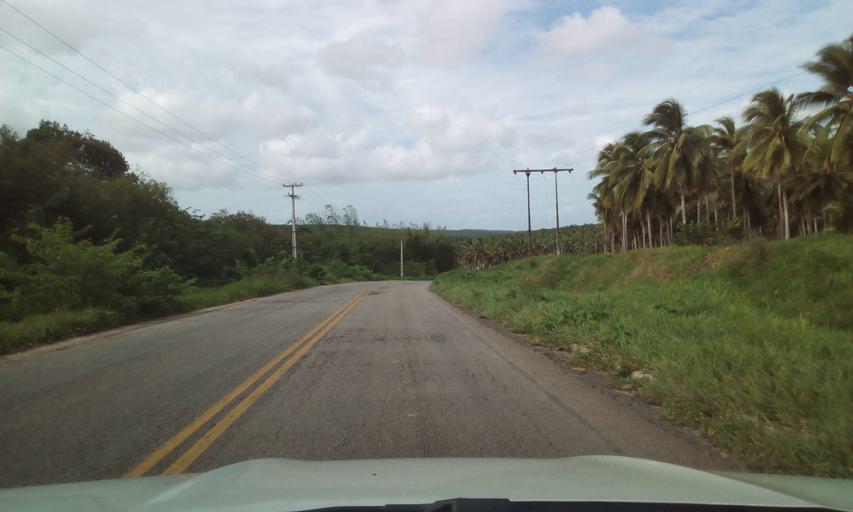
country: BR
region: Paraiba
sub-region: Cabedelo
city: Cabedelo
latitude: -6.9634
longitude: -34.9573
